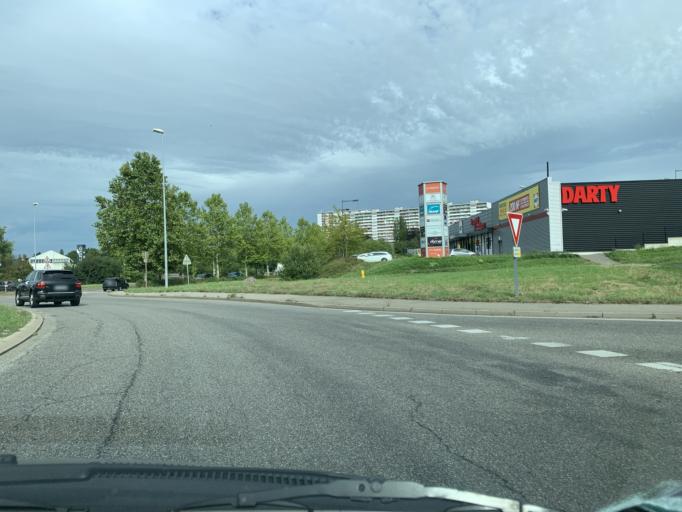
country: FR
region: Alsace
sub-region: Departement du Haut-Rhin
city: Morschwiller-le-Bas
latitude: 47.7366
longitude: 7.2888
